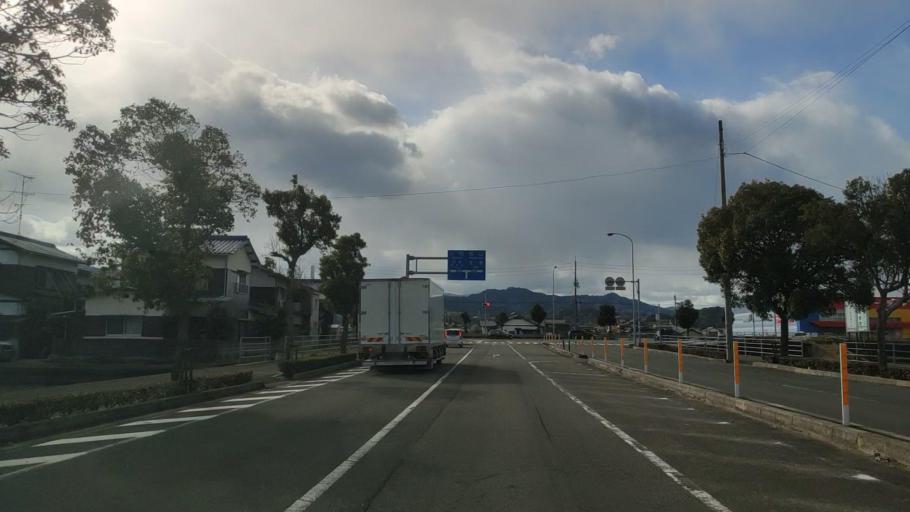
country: JP
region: Ehime
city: Saijo
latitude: 34.0382
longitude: 132.9972
